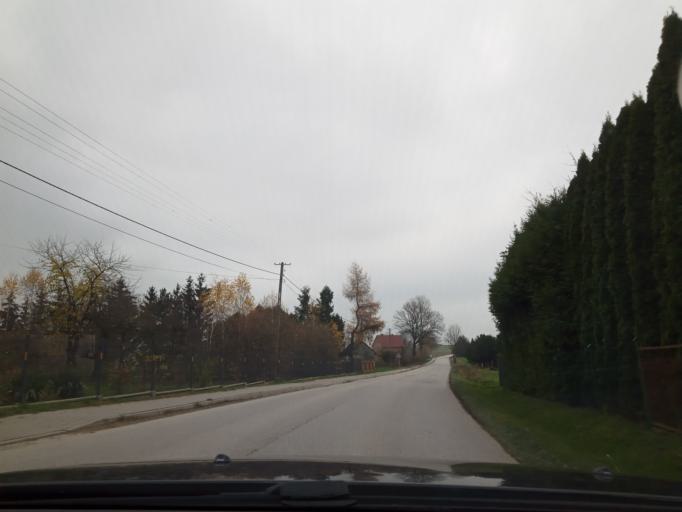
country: PL
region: Swietokrzyskie
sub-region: Powiat jedrzejowski
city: Imielno
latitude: 50.6098
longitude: 20.3916
